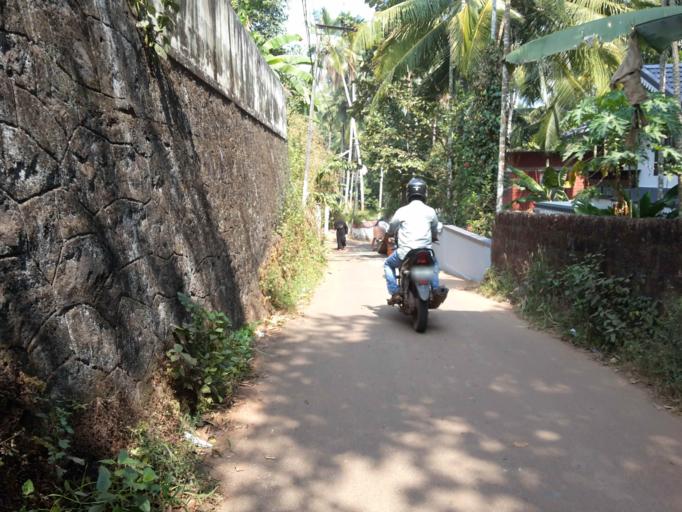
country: IN
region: Kerala
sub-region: Kozhikode
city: Kunnamangalam
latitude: 11.2976
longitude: 75.8444
